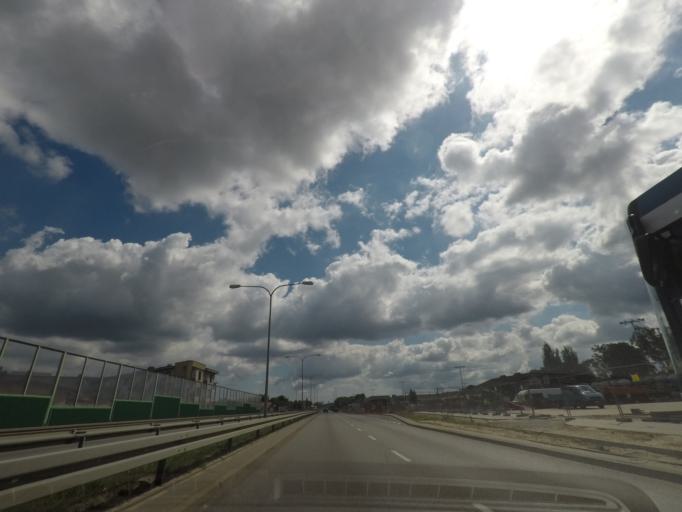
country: PL
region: Pomeranian Voivodeship
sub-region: Powiat wejherowski
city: Wejherowo
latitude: 54.6071
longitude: 18.2283
